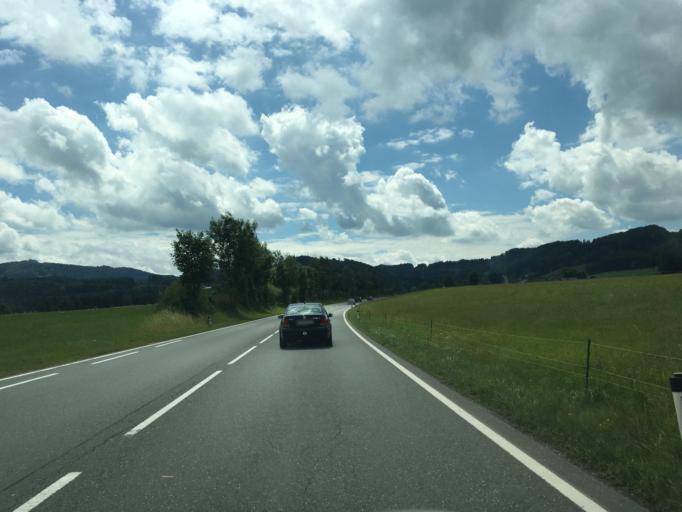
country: AT
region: Salzburg
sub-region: Politischer Bezirk Salzburg-Umgebung
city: Hof bei Salzburg
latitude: 47.8471
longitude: 13.2189
